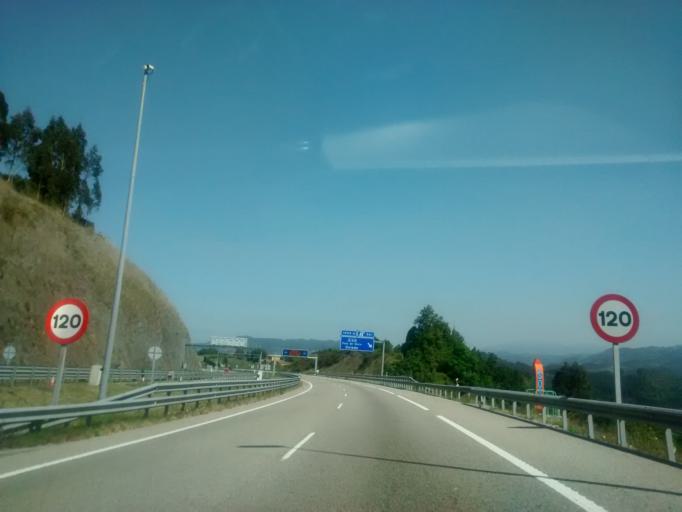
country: ES
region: Asturias
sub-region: Province of Asturias
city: Arriba
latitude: 43.4626
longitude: -5.5123
